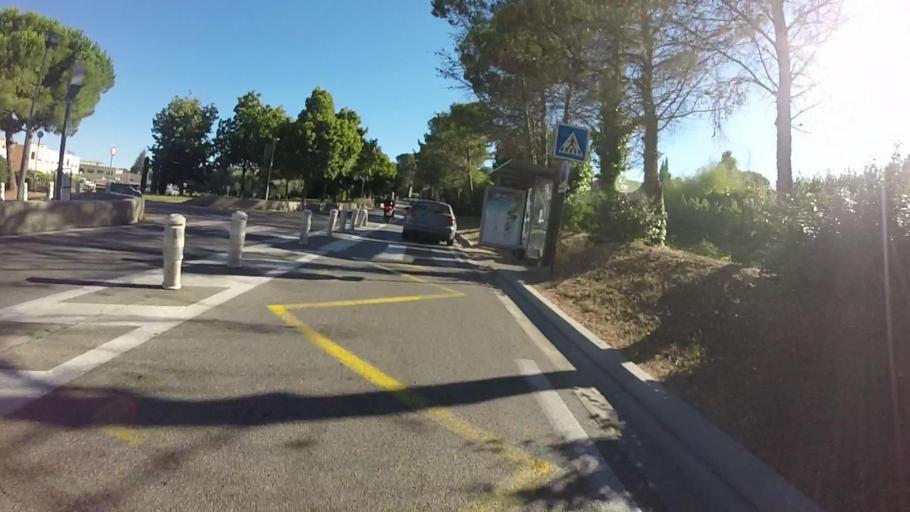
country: FR
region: Provence-Alpes-Cote d'Azur
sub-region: Departement des Alpes-Maritimes
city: Mougins
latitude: 43.6097
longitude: 7.0107
